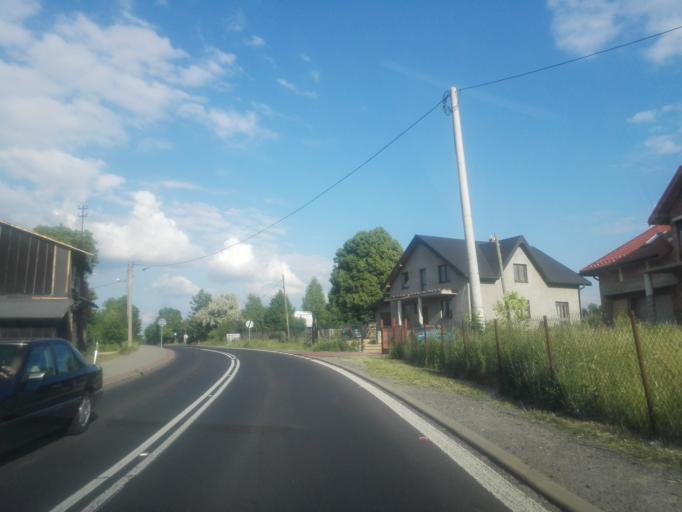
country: PL
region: Silesian Voivodeship
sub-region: Powiat czestochowski
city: Potok Zloty
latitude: 50.7240
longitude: 19.4231
